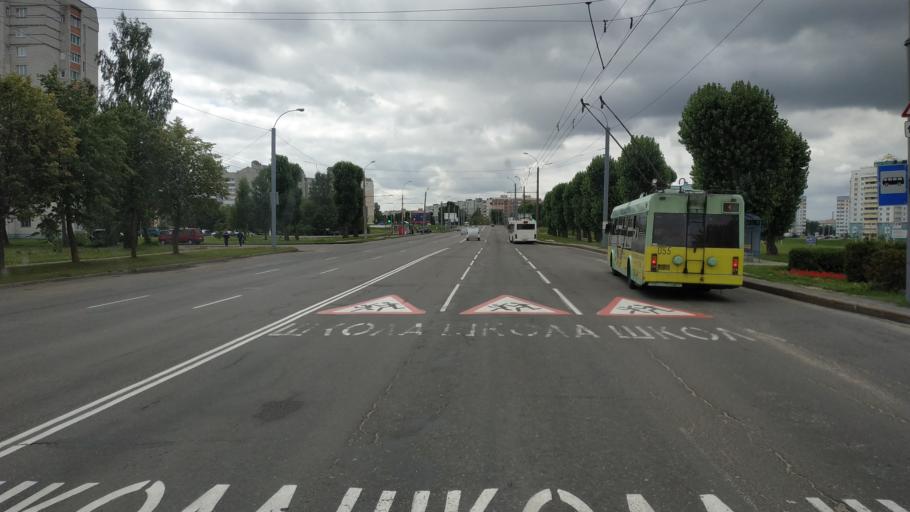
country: BY
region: Mogilev
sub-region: Mahilyowski Rayon
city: Veyno
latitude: 53.8790
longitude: 30.3882
